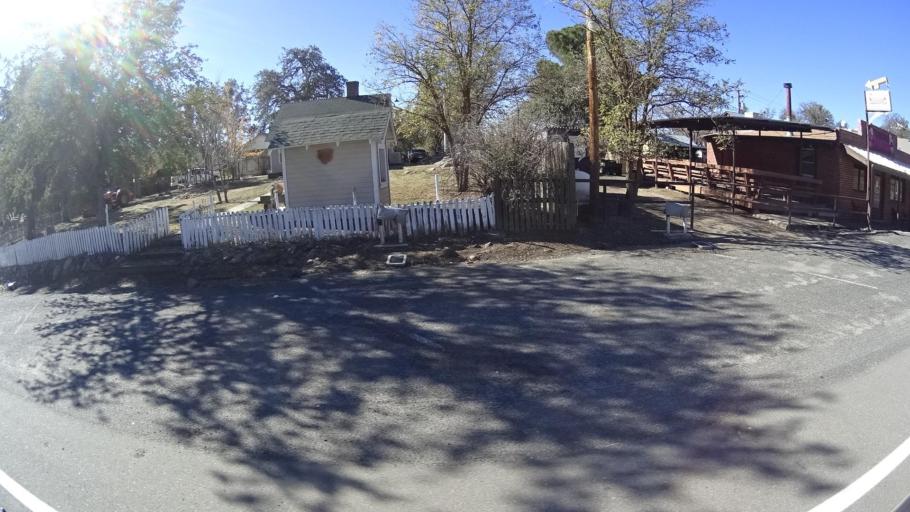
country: US
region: California
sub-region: Kern County
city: Alta Sierra
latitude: 35.7282
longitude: -118.7028
